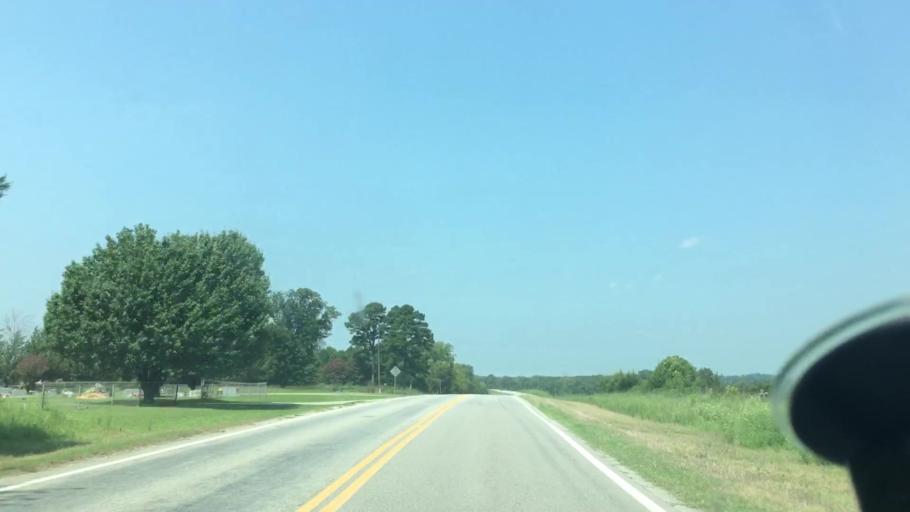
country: US
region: Oklahoma
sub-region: Atoka County
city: Atoka
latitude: 34.2816
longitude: -95.9520
